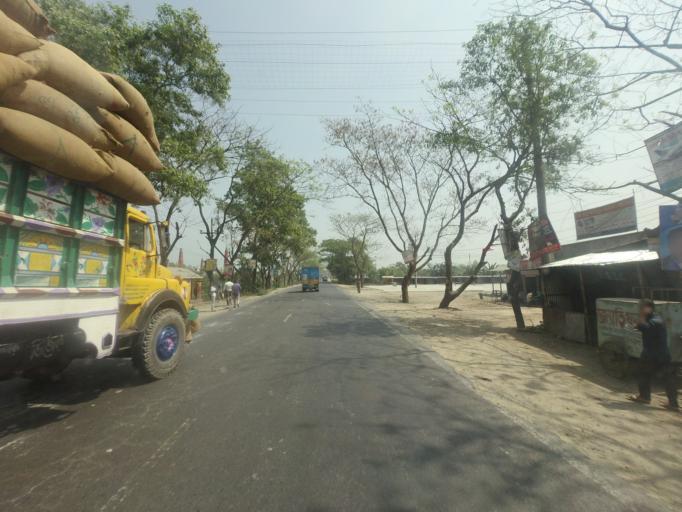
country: BD
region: Dhaka
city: Bhairab Bazar
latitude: 24.0416
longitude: 91.0443
